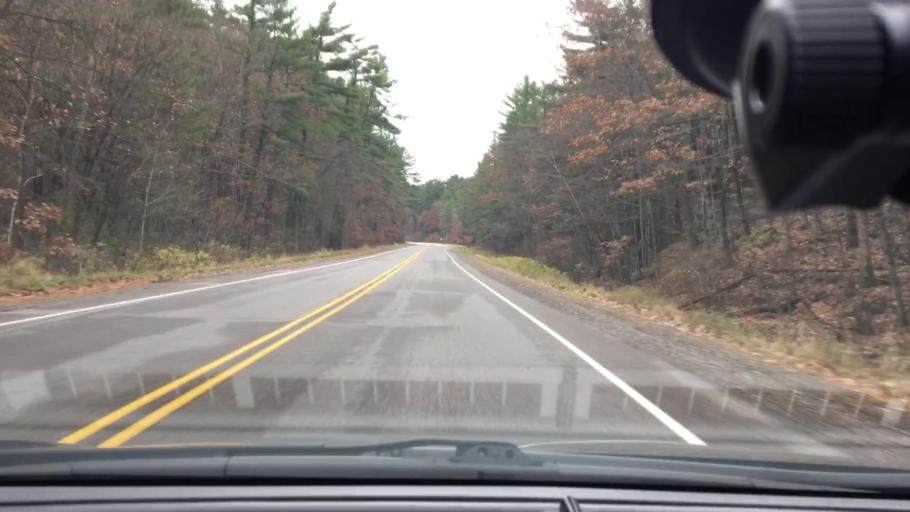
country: US
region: Wisconsin
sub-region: Columbia County
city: Wisconsin Dells
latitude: 43.6436
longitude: -89.8045
